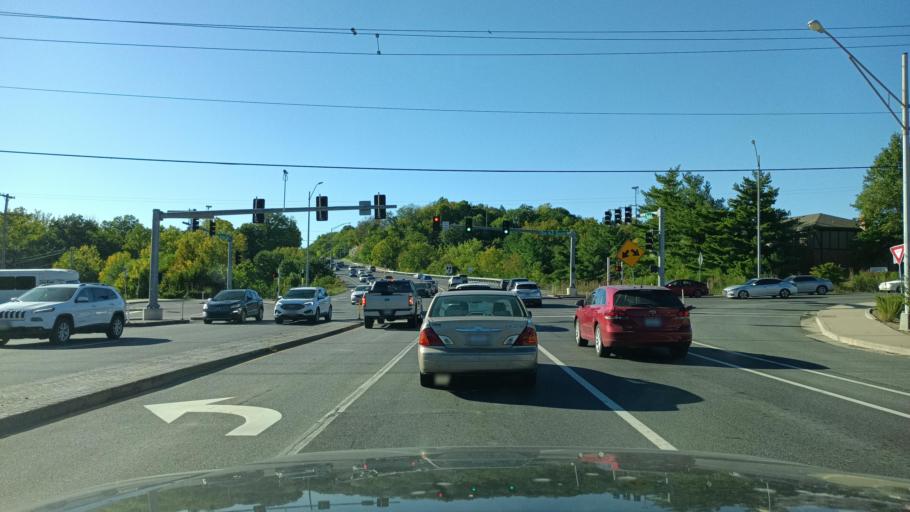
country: US
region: Missouri
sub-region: Boone County
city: Columbia
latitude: 38.9318
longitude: -92.3109
